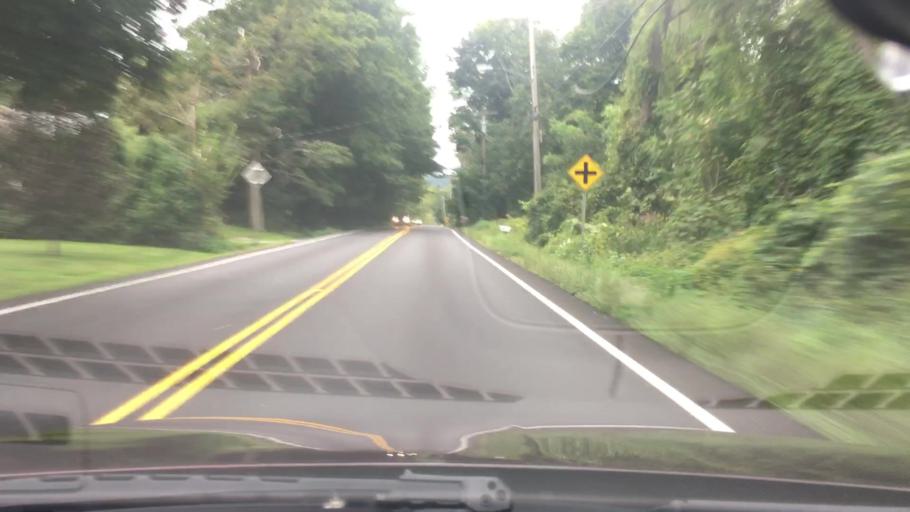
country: US
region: New York
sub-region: Dutchess County
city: Dover Plains
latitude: 41.8547
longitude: -73.5407
